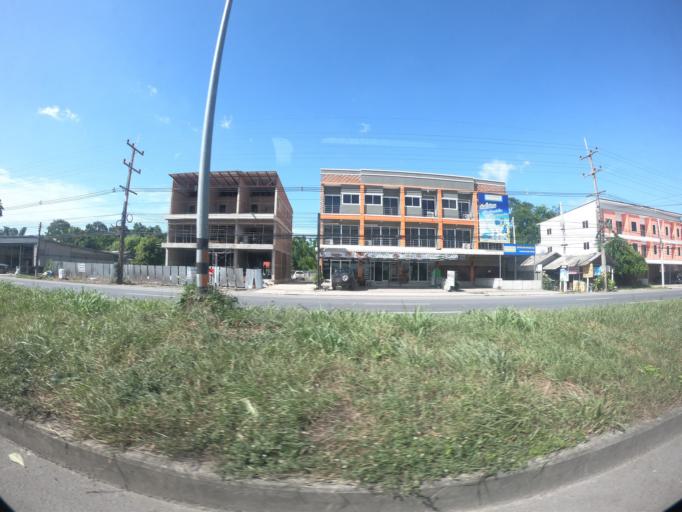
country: TH
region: Nakhon Nayok
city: Ban Na
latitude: 14.2563
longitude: 101.0817
